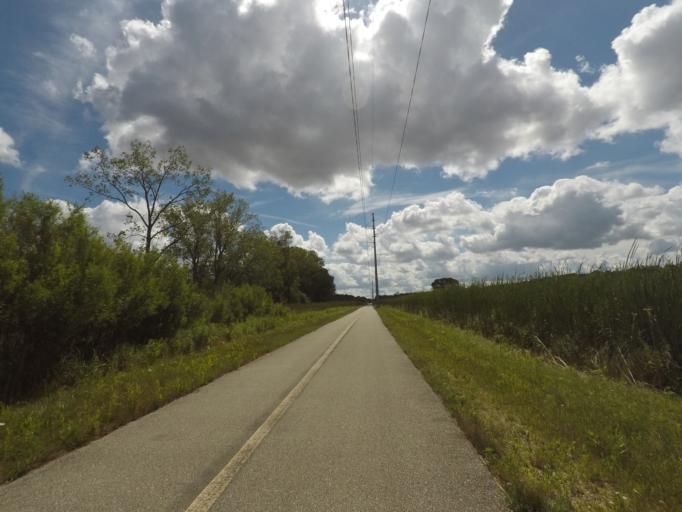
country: US
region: Wisconsin
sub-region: Waukesha County
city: Pewaukee
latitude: 43.0564
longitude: -88.2902
